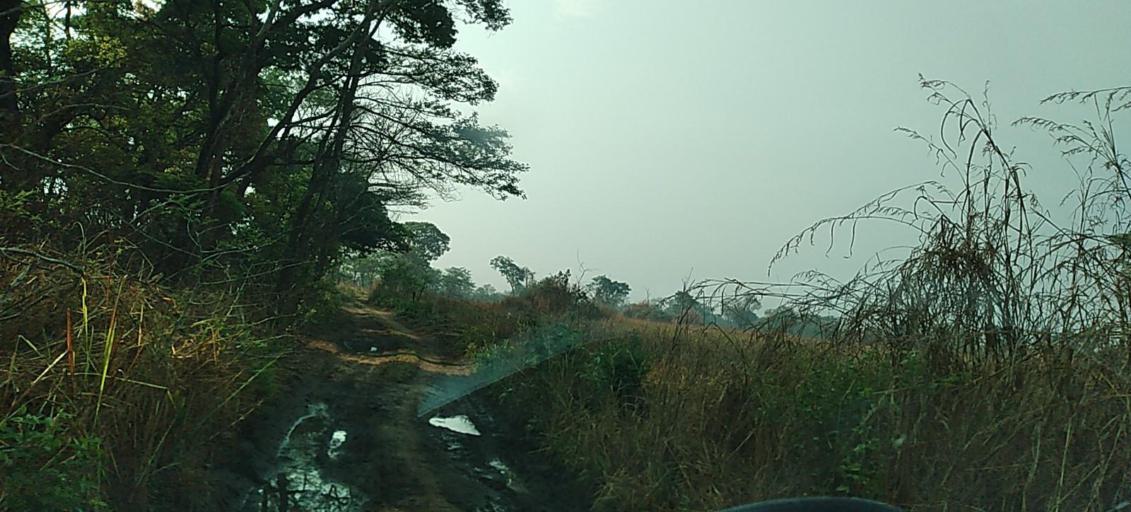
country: ZM
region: North-Western
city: Solwezi
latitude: -12.3760
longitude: 26.5620
